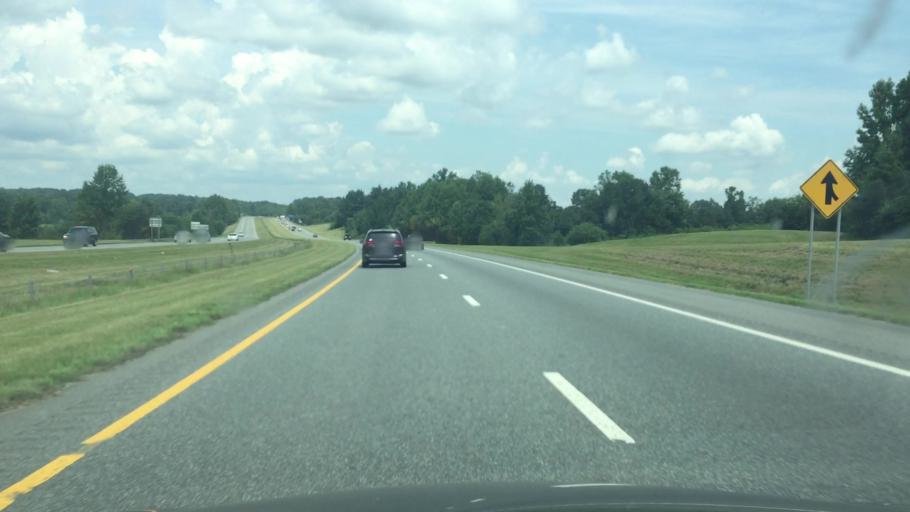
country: US
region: North Carolina
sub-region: Montgomery County
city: Biscoe
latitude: 35.4909
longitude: -79.7799
